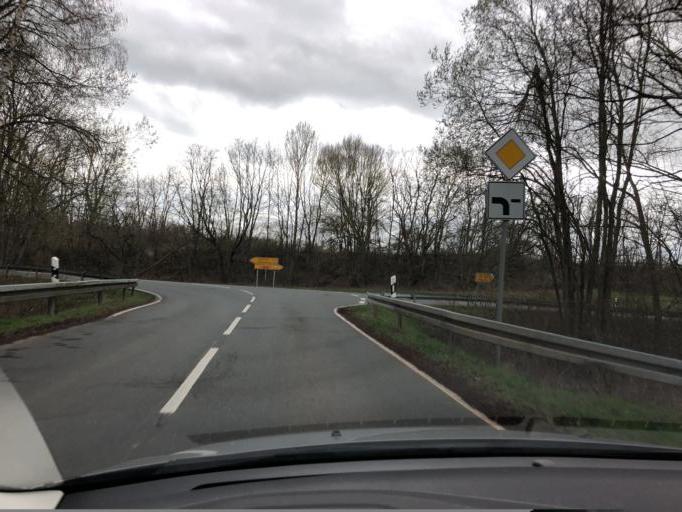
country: DE
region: Saxony-Anhalt
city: Hohenmolsen
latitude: 51.1597
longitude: 12.1260
